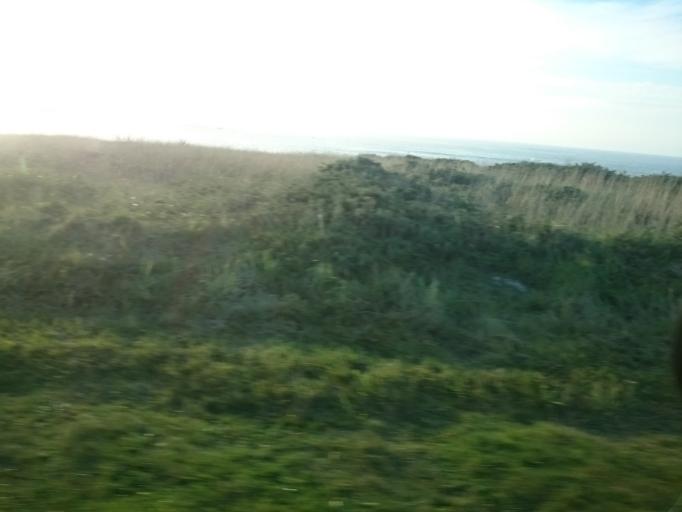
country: FR
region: Brittany
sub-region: Departement du Finistere
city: Landunvez
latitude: 48.5387
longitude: -4.7484
